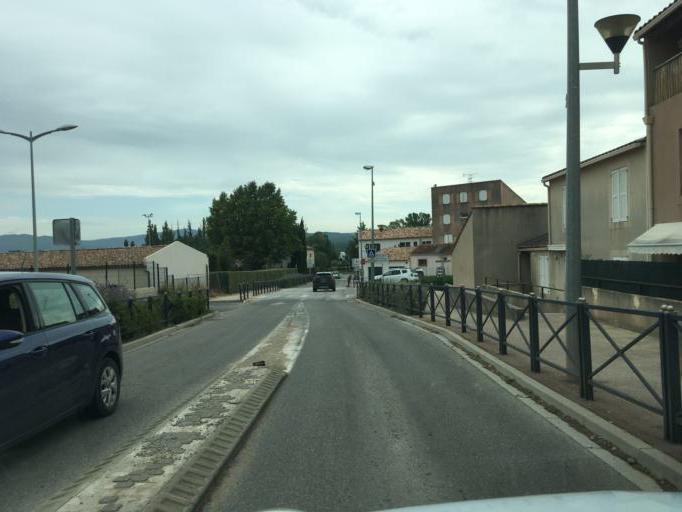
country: FR
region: Provence-Alpes-Cote d'Azur
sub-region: Departement des Bouches-du-Rhone
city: Rousset
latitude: 43.4806
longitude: 5.6241
